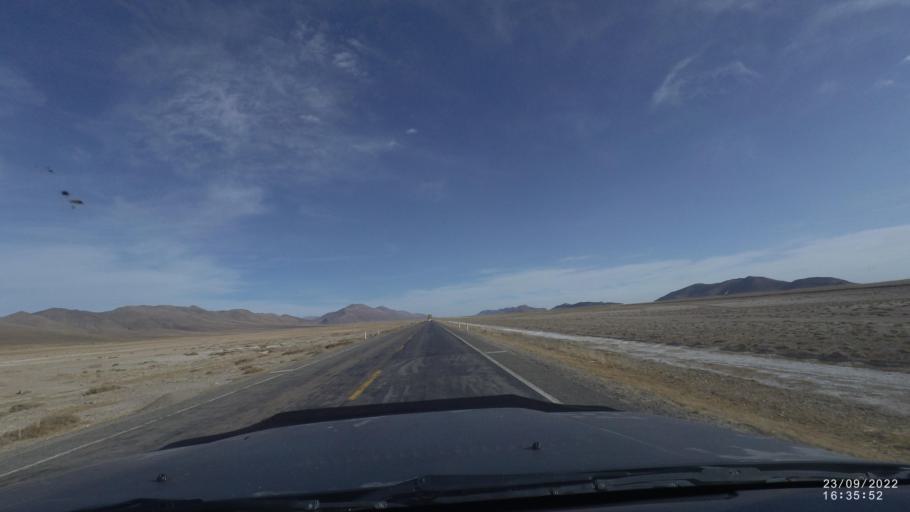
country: BO
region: Oruro
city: Machacamarca
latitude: -18.2110
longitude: -67.0097
